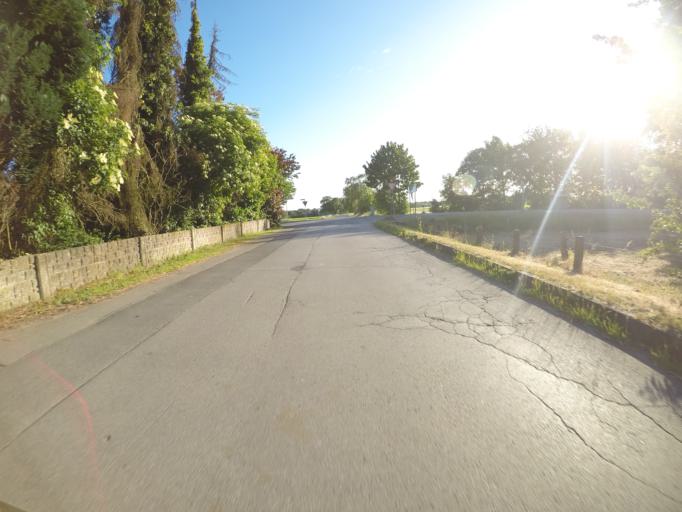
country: DE
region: North Rhine-Westphalia
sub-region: Regierungsbezirk Dusseldorf
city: Schermbeck
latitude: 51.7186
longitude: 6.8720
